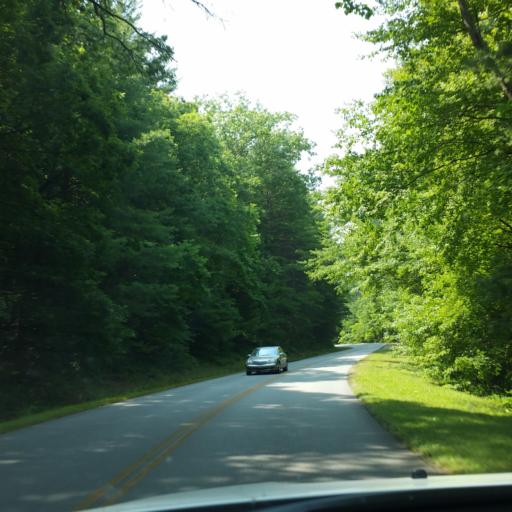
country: US
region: North Carolina
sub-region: Buncombe County
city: Biltmore Forest
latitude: 35.5043
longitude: -82.5583
